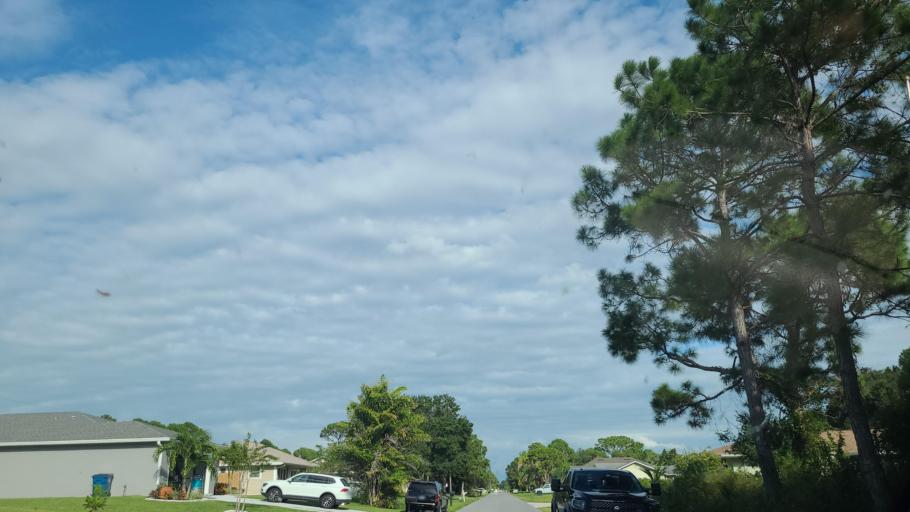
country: US
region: Florida
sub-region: Brevard County
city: Palm Bay
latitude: 27.9837
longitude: -80.6605
